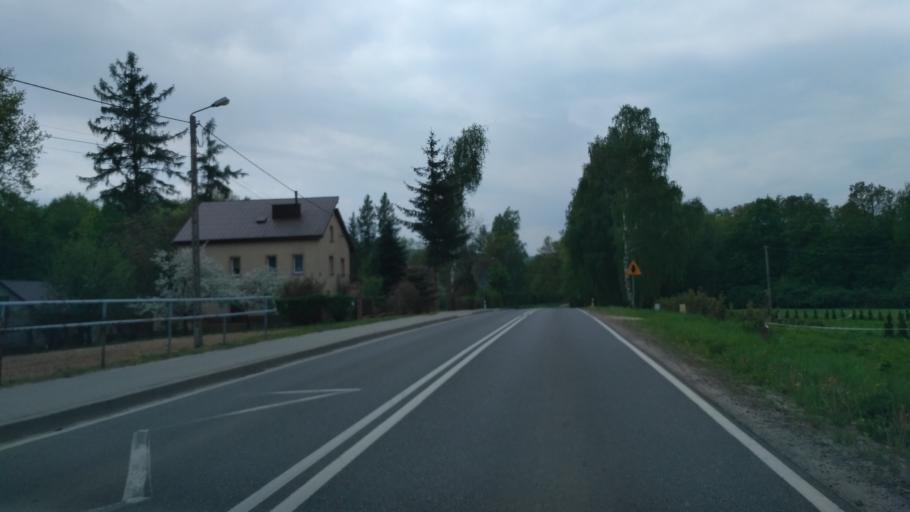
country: PL
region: Lesser Poland Voivodeship
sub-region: Powiat tarnowski
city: Tarnowiec
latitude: 49.9633
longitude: 20.9922
